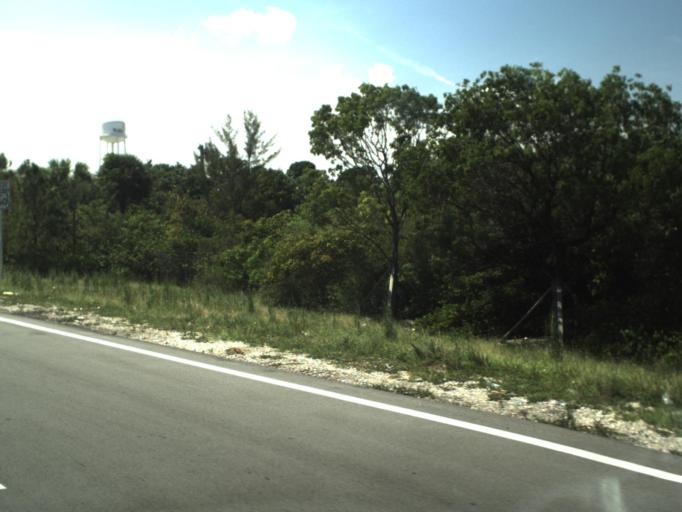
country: US
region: Florida
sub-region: Miami-Dade County
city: Ives Estates
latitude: 25.9417
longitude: -80.1868
